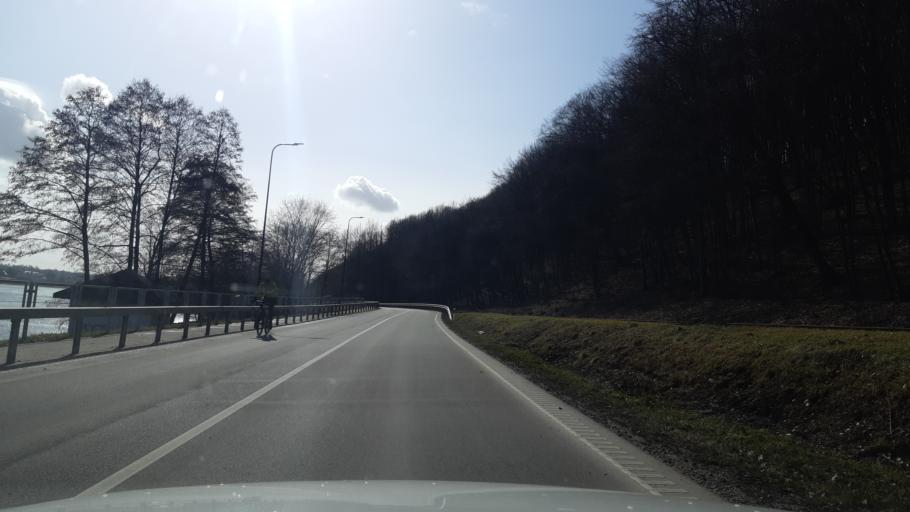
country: LT
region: Kauno apskritis
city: Dainava (Kaunas)
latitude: 54.8859
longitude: 23.9561
